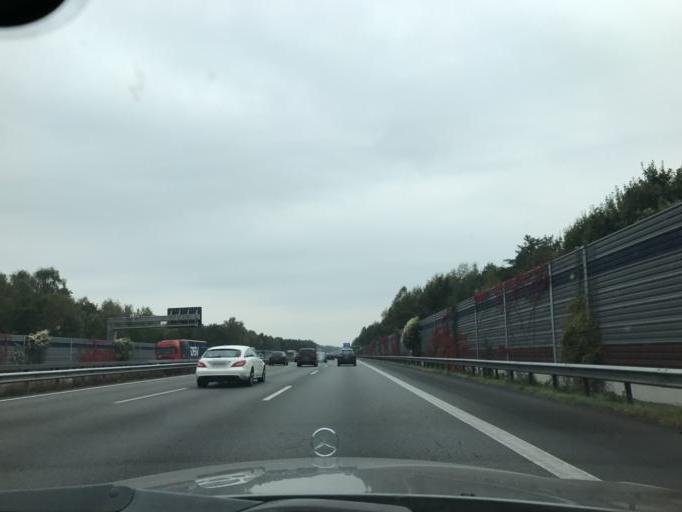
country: DE
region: Lower Saxony
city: Reessum
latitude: 53.0993
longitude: 9.1888
